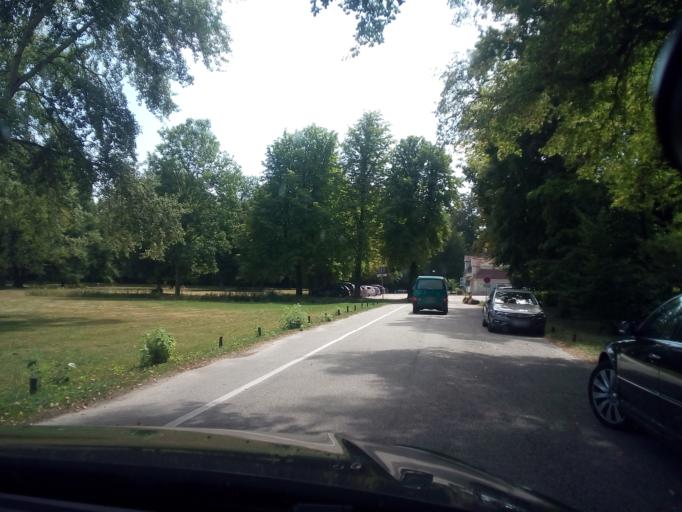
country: DE
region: Baden-Wuerttemberg
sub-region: Karlsruhe Region
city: Kuppenheim
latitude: 48.8230
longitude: 8.2359
